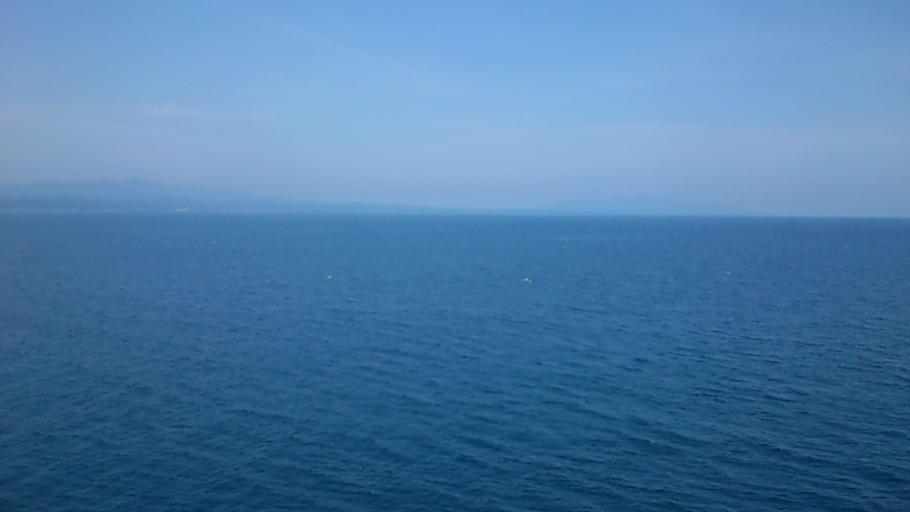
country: JP
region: Aomori
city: Aomori Shi
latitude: 40.8619
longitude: 140.7354
